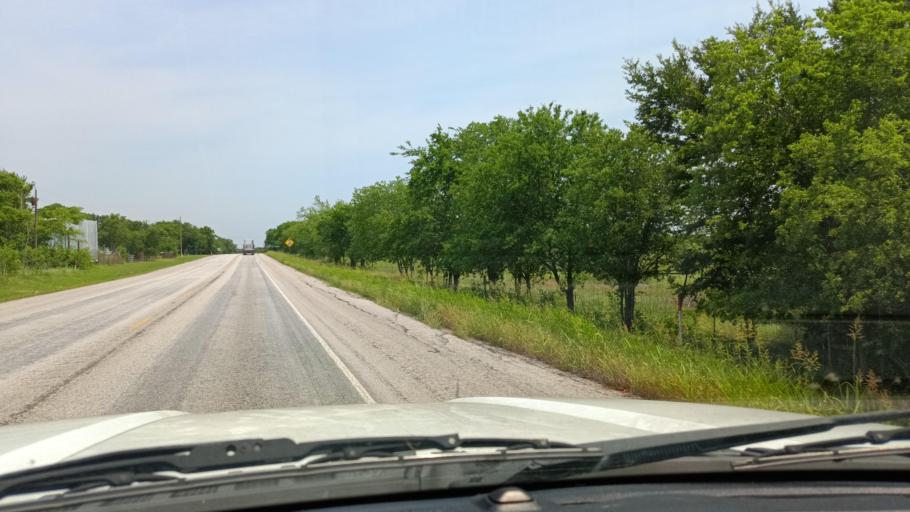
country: US
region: Texas
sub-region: Bell County
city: Rogers
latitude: 30.9452
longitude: -97.2453
